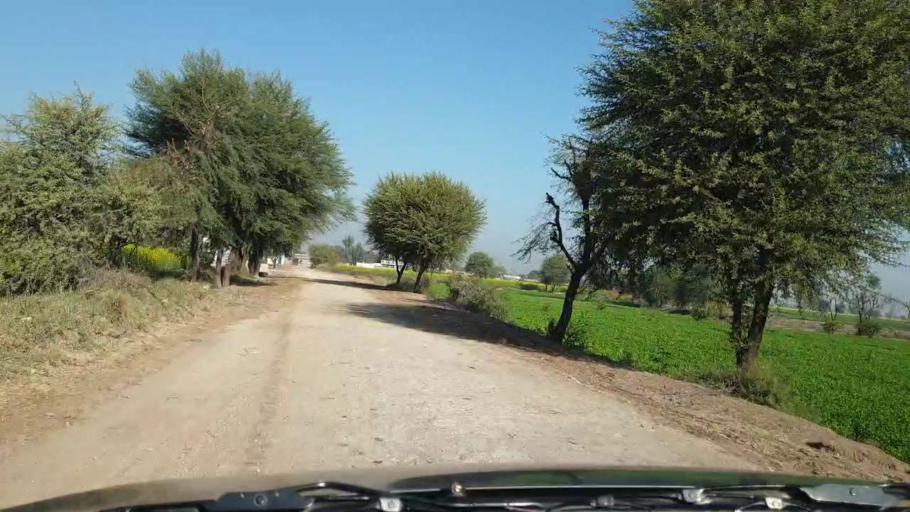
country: PK
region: Sindh
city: Jhol
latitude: 25.9383
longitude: 68.8412
